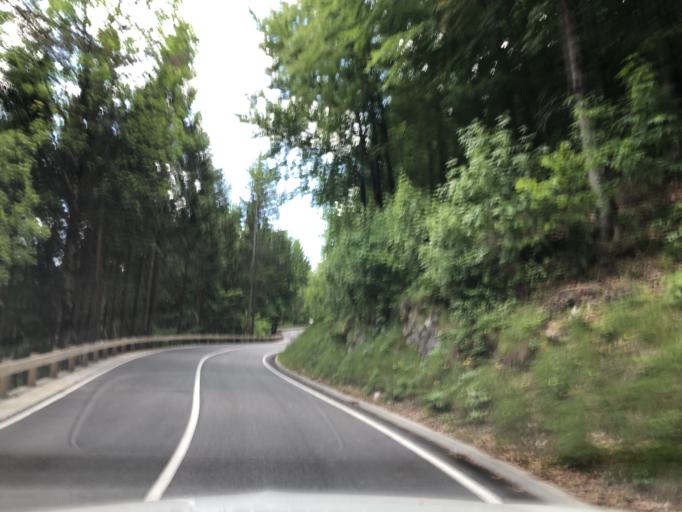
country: IT
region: Friuli Venezia Giulia
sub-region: Provincia di Udine
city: Tarvisio
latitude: 46.4177
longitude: 13.6236
